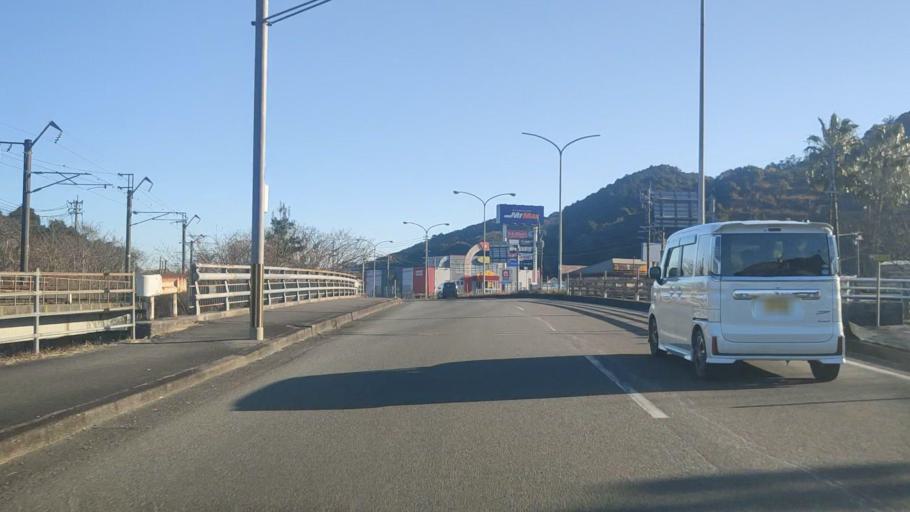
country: JP
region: Miyazaki
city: Nobeoka
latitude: 32.4494
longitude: 131.6383
